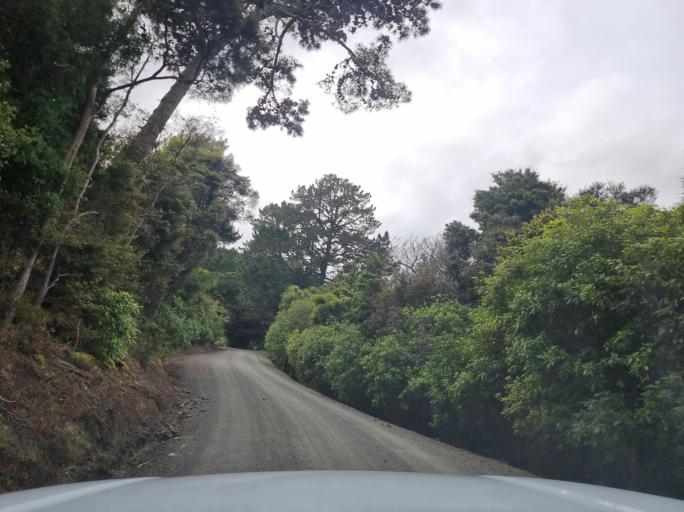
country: NZ
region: Northland
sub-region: Whangarei
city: Ruakaka
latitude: -36.1073
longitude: 174.2075
